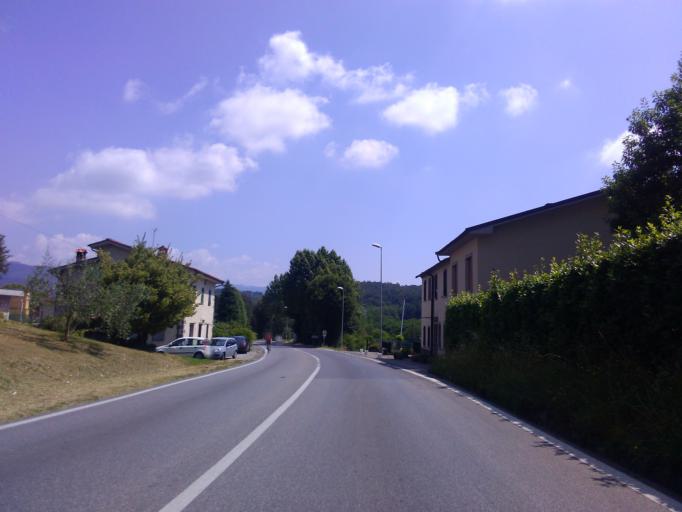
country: IT
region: Tuscany
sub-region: Provincia di Lucca
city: Porcari
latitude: 43.8656
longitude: 10.6344
